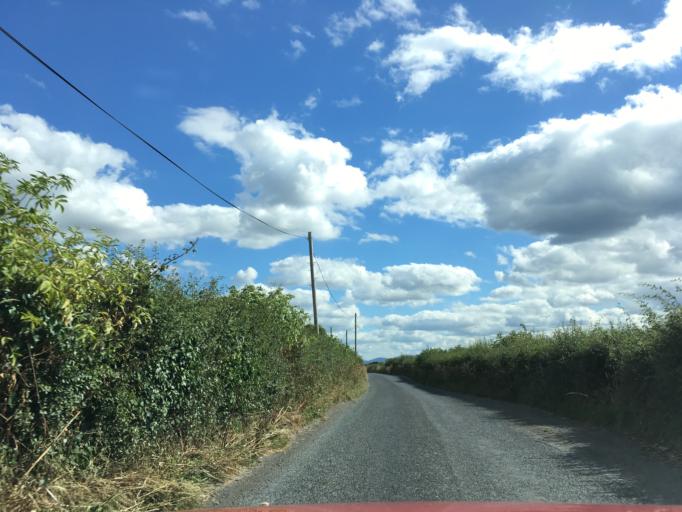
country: IE
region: Munster
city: Cashel
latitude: 52.4657
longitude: -7.9756
